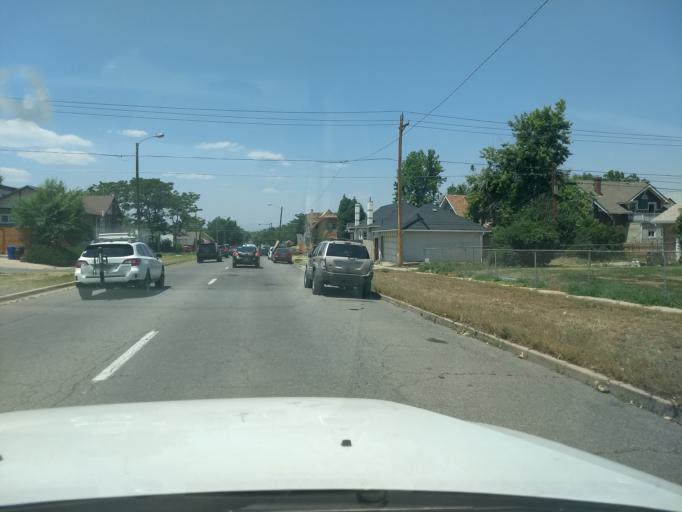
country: US
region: Colorado
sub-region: Denver County
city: Denver
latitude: 39.7620
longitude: -104.9576
